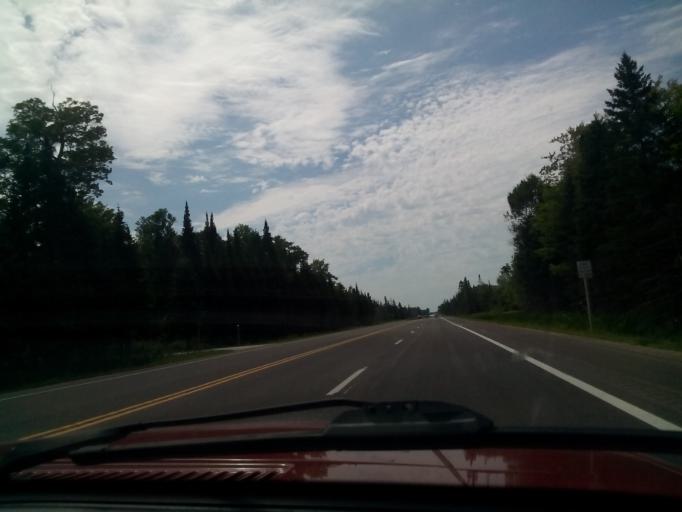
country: US
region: Michigan
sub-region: Schoolcraft County
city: Manistique
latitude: 46.0267
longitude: -85.9834
